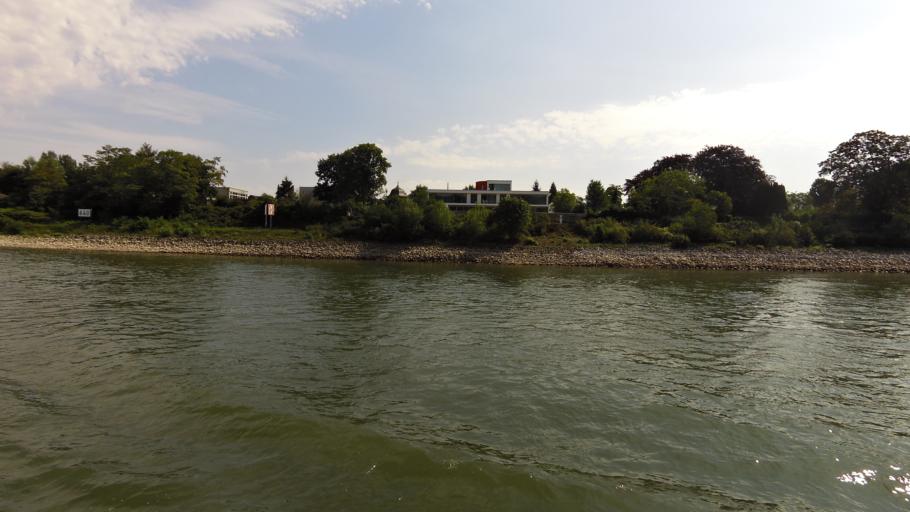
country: DE
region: North Rhine-Westphalia
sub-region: Regierungsbezirk Koln
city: Bad Honnef
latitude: 50.6292
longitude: 7.2130
